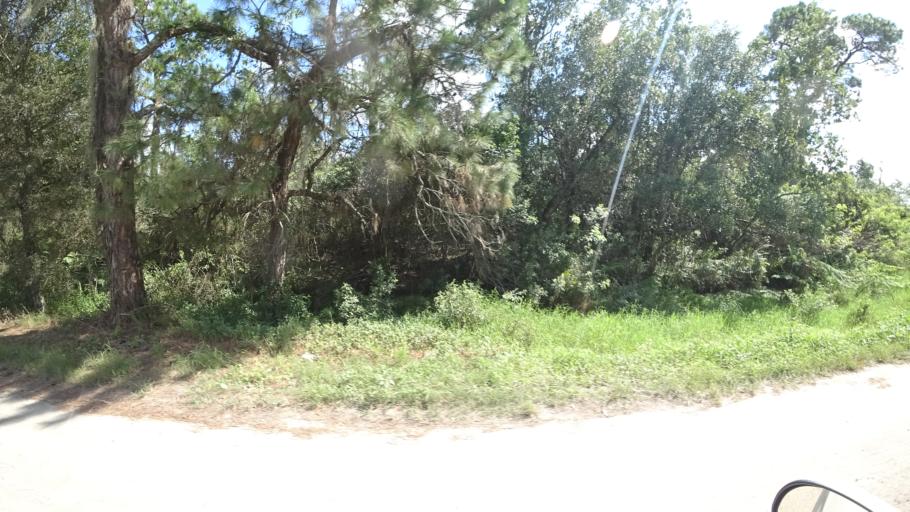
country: US
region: Florida
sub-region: DeSoto County
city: Arcadia
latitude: 27.3225
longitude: -82.1303
